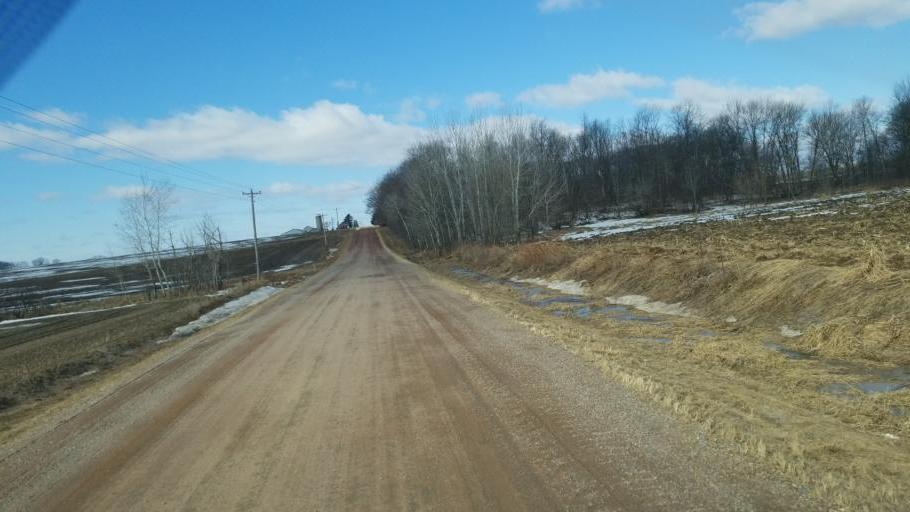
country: US
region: Wisconsin
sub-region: Clark County
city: Loyal
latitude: 44.6834
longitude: -90.4523
